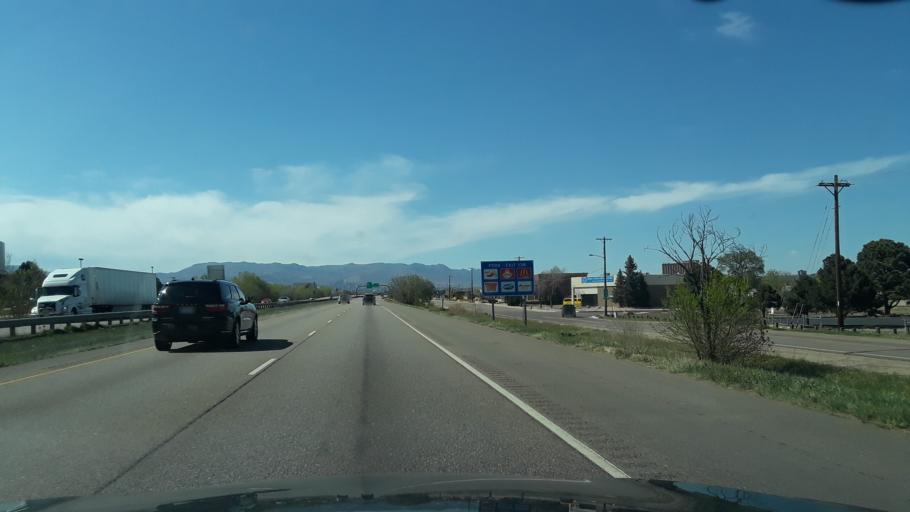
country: US
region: Colorado
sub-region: El Paso County
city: Stratmoor
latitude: 38.7873
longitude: -104.7914
